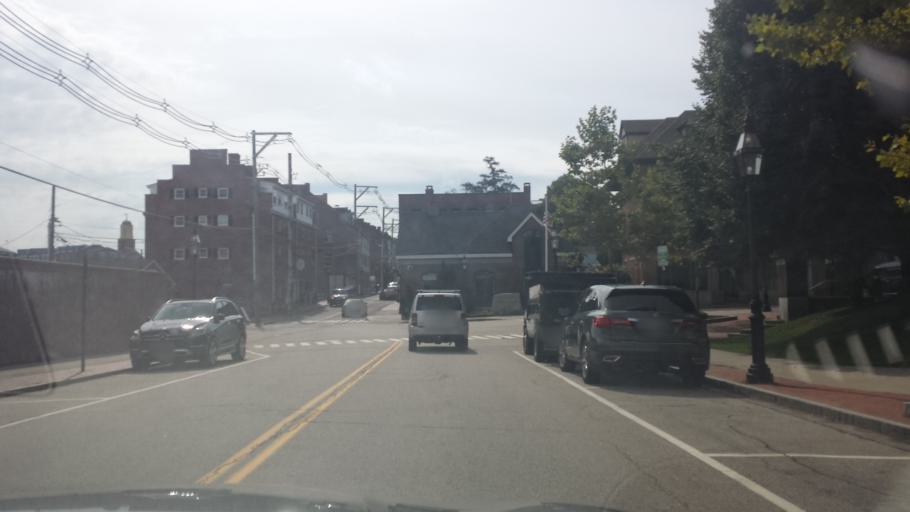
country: US
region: New Hampshire
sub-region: Rockingham County
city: Portsmouth
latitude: 43.0800
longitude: -70.7598
